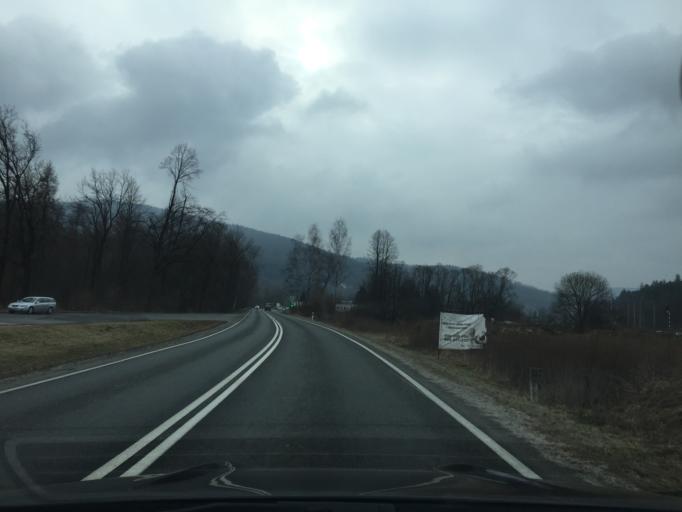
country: PL
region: Lesser Poland Voivodeship
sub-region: Powiat suski
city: Zembrzyce
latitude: 49.7625
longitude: 19.5975
